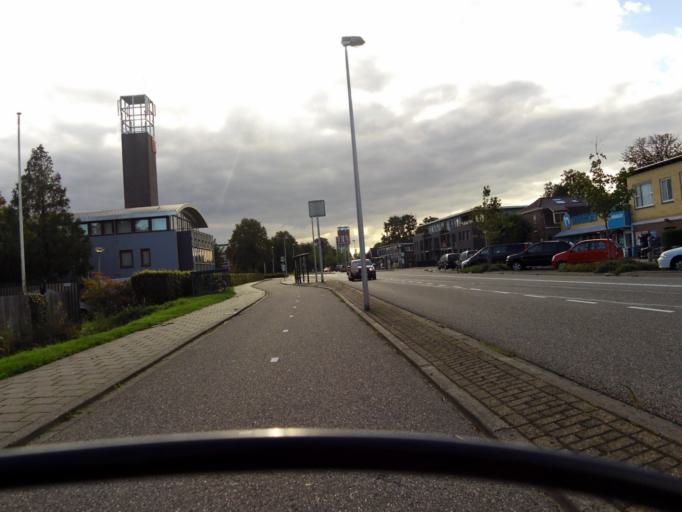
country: NL
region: South Holland
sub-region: Gemeente Alphen aan den Rijn
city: Alphen aan den Rijn
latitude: 52.1299
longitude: 4.5895
